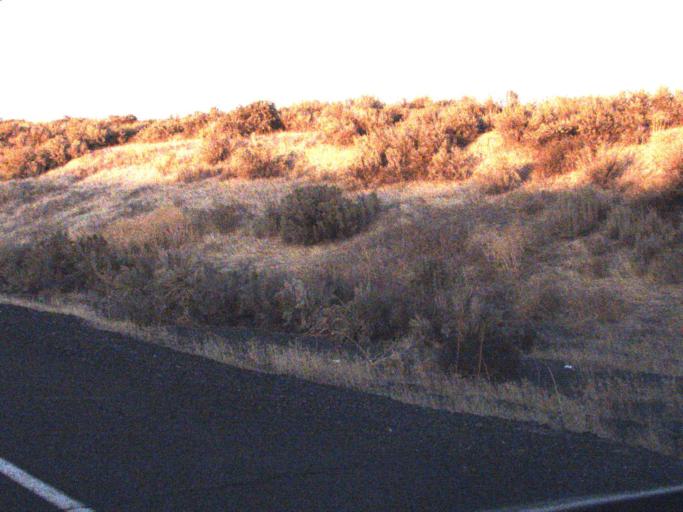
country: US
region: Washington
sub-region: Adams County
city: Ritzville
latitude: 47.0943
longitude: -118.6680
